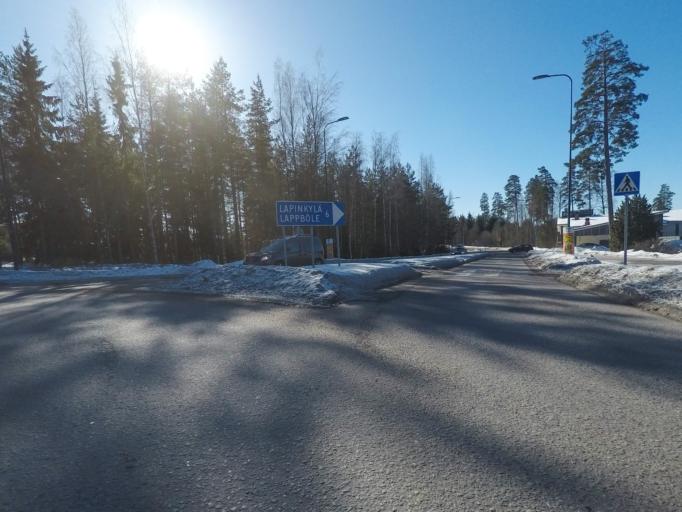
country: FI
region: Uusimaa
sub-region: Helsinki
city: Kirkkonummi
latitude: 60.2695
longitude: 24.4458
